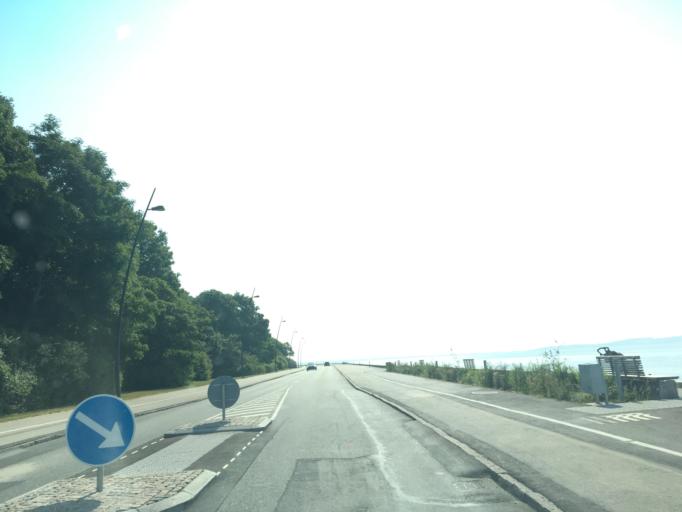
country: DK
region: North Denmark
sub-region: Thisted Kommune
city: Thisted
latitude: 56.9514
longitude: 8.6848
